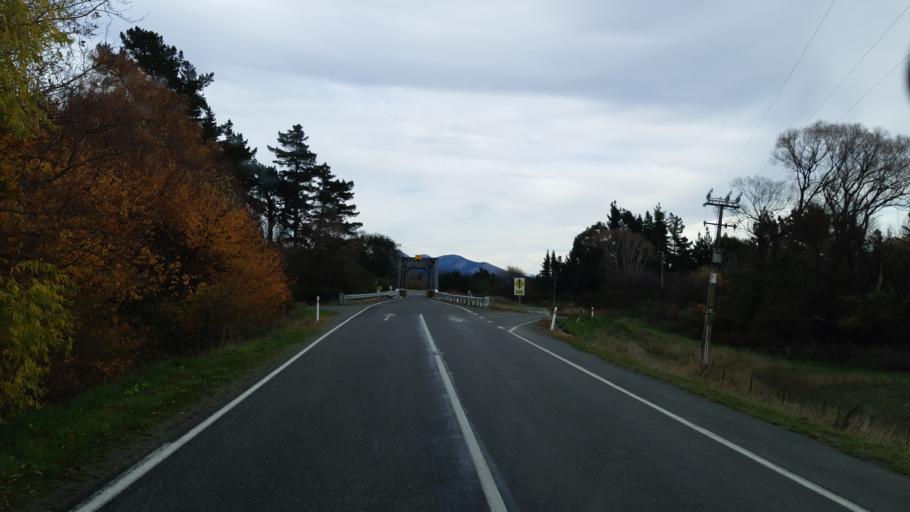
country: NZ
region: Tasman
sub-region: Tasman District
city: Brightwater
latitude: -41.6347
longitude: 173.3248
